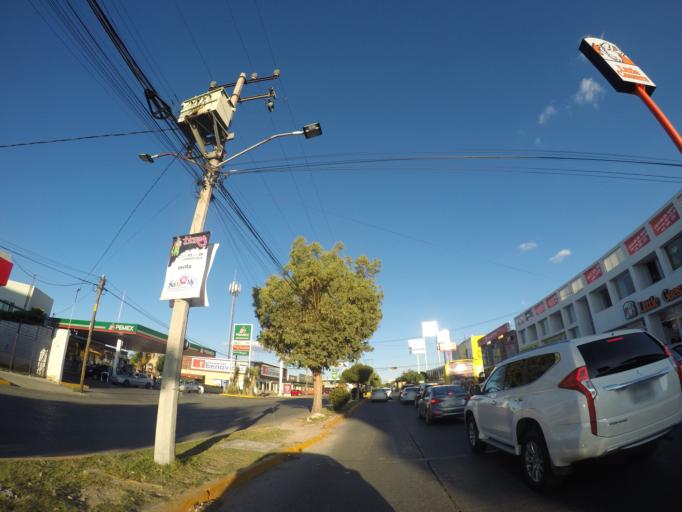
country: MX
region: San Luis Potosi
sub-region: San Luis Potosi
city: San Luis Potosi
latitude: 22.1357
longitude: -100.9810
